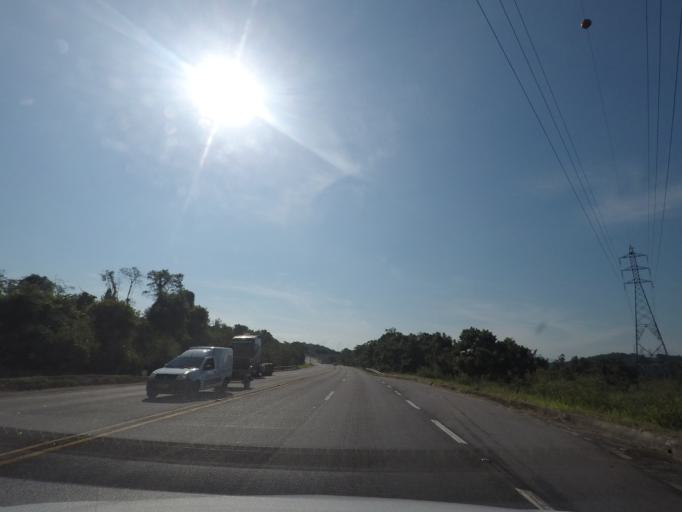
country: BR
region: Parana
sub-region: Paranagua
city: Paranagua
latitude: -25.5743
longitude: -48.6129
